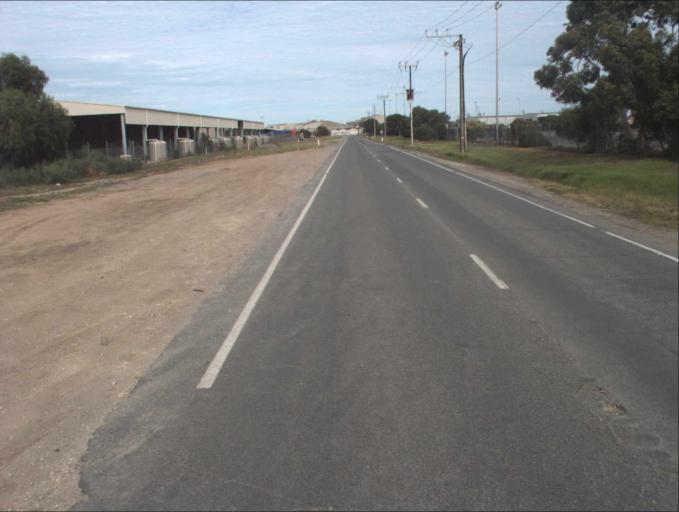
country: AU
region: South Australia
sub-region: Port Adelaide Enfield
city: Birkenhead
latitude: -34.8275
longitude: 138.5194
